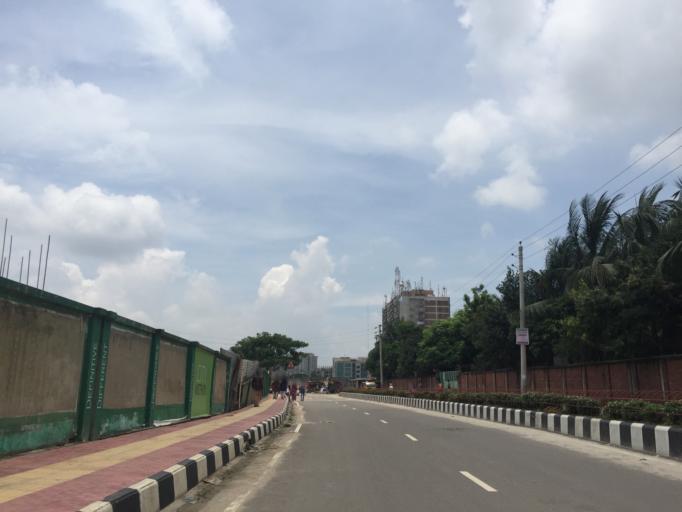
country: BD
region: Dhaka
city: Azimpur
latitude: 23.8040
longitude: 90.3839
